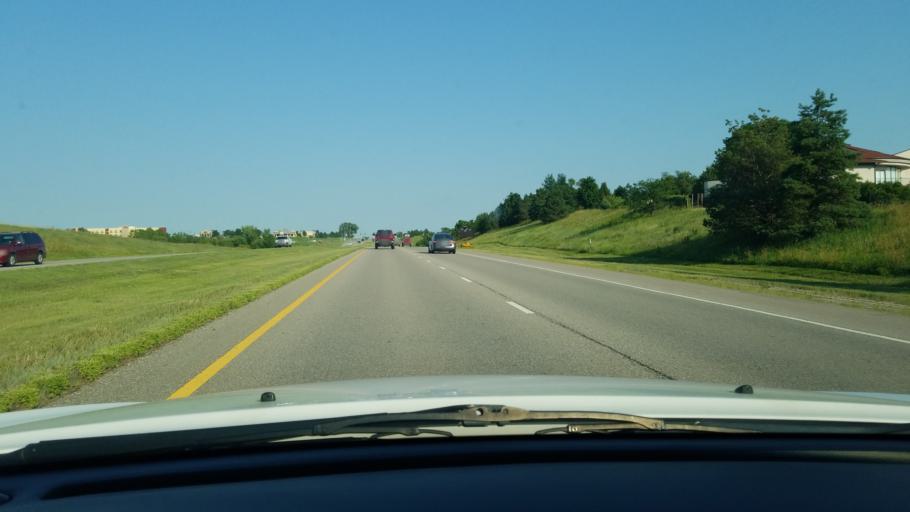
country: US
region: Nebraska
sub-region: Lancaster County
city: Lincoln
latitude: 40.7394
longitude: -96.6130
